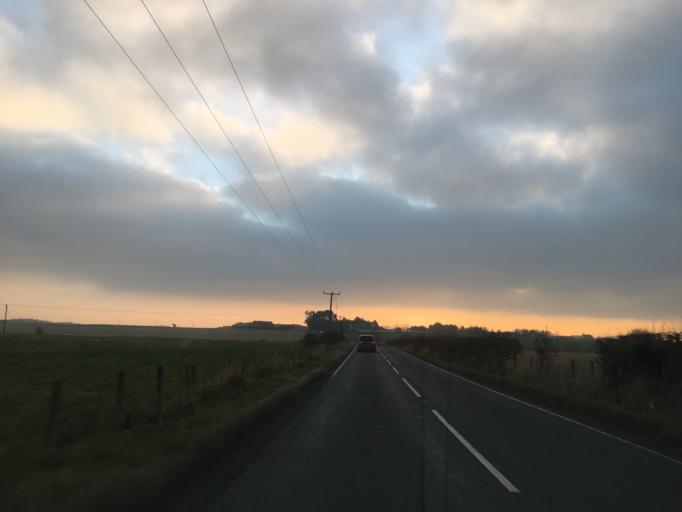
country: GB
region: Scotland
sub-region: Fife
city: Strathkinness
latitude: 56.2661
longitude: -2.8515
